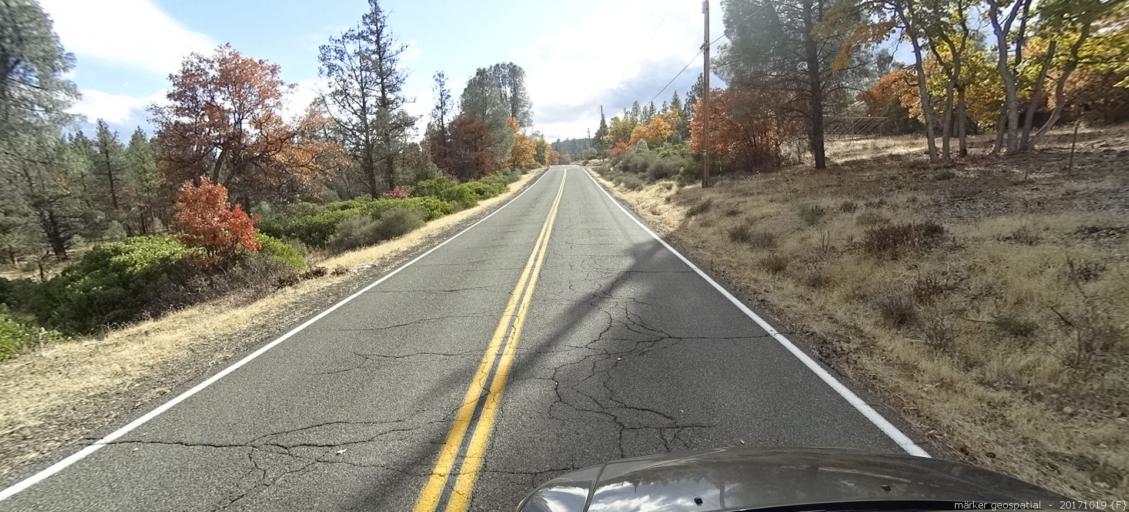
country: US
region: California
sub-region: Shasta County
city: Burney
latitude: 40.9623
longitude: -121.4366
